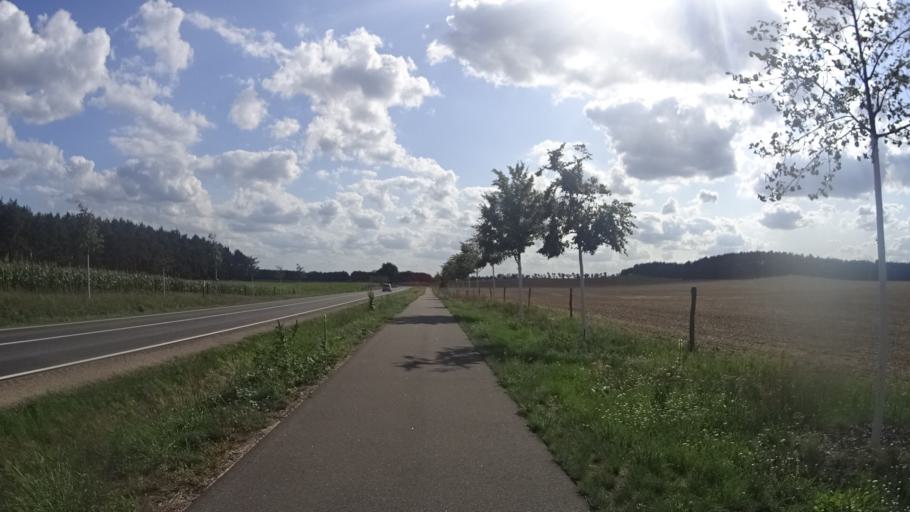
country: DE
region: Brandenburg
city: Rhinow
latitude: 52.6997
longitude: 12.3694
